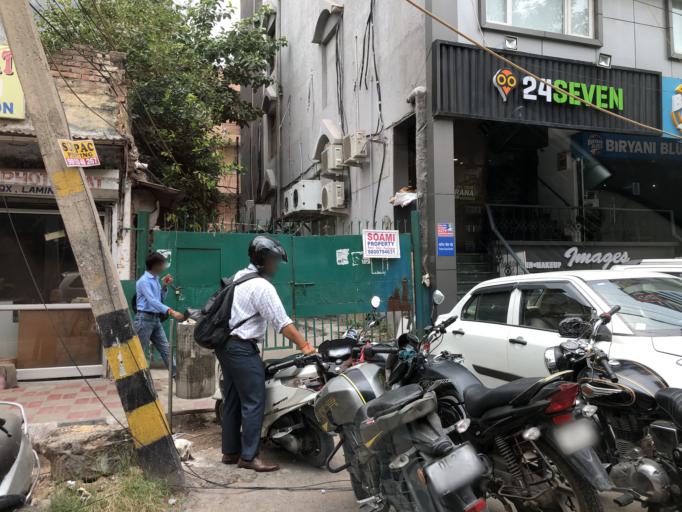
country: IN
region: NCT
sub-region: New Delhi
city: New Delhi
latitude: 28.5669
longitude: 77.2464
